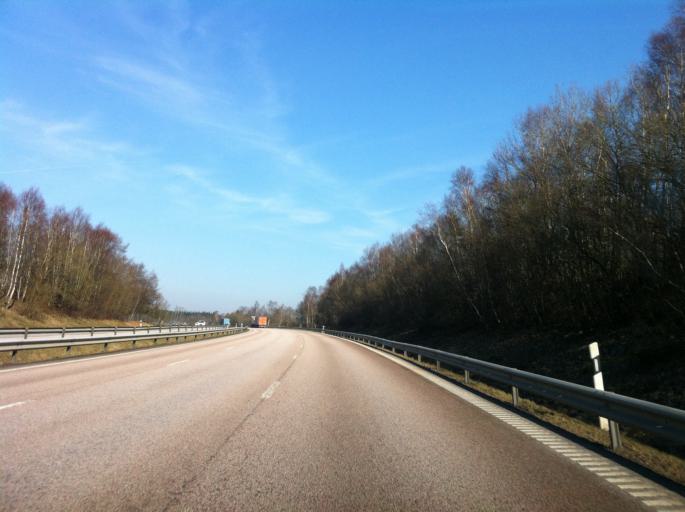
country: SE
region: Skane
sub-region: Bastads Kommun
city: Bastad
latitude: 56.3530
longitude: 12.9324
